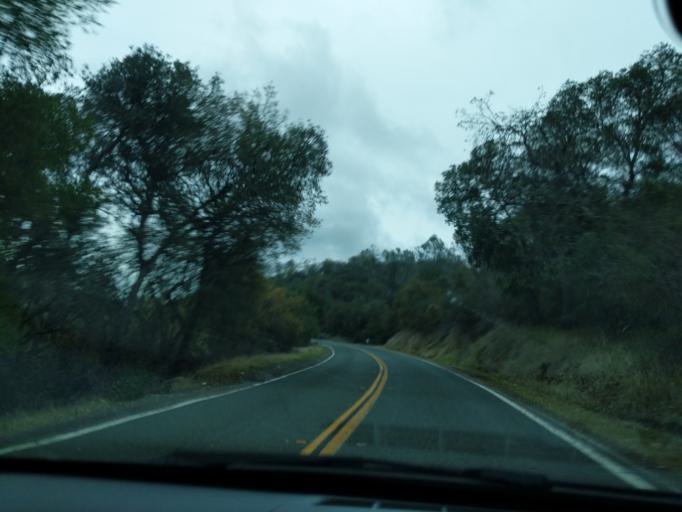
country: US
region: California
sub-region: Monterey County
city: Soledad
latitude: 36.5811
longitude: -121.1920
